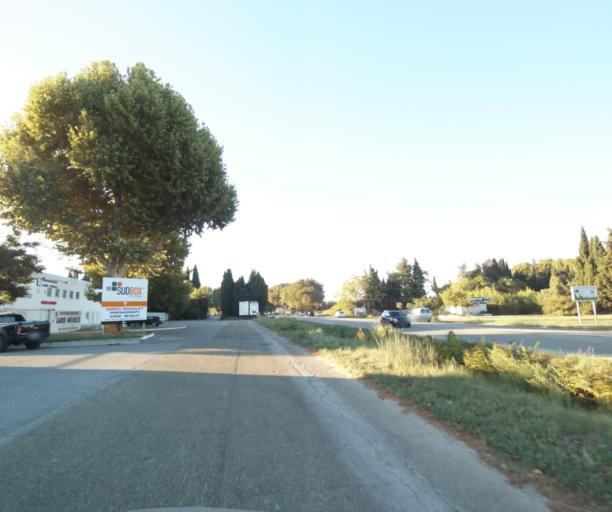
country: FR
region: Languedoc-Roussillon
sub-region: Departement du Gard
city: Caissargues
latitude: 43.8084
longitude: 4.4029
